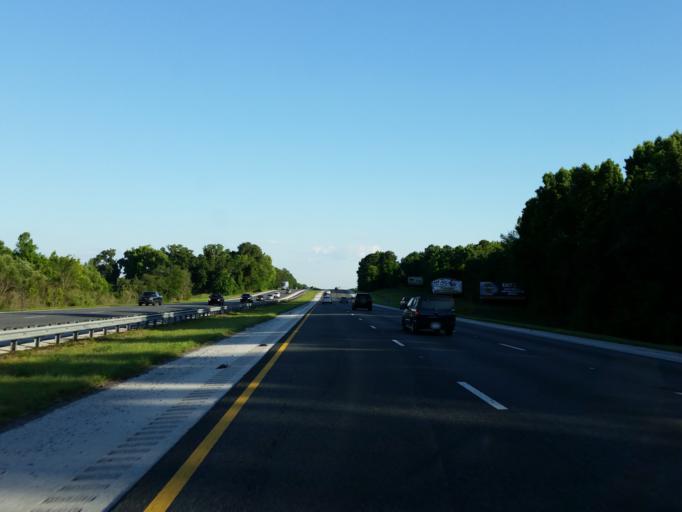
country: US
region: Florida
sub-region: Marion County
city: Citra
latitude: 29.3364
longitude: -82.2160
